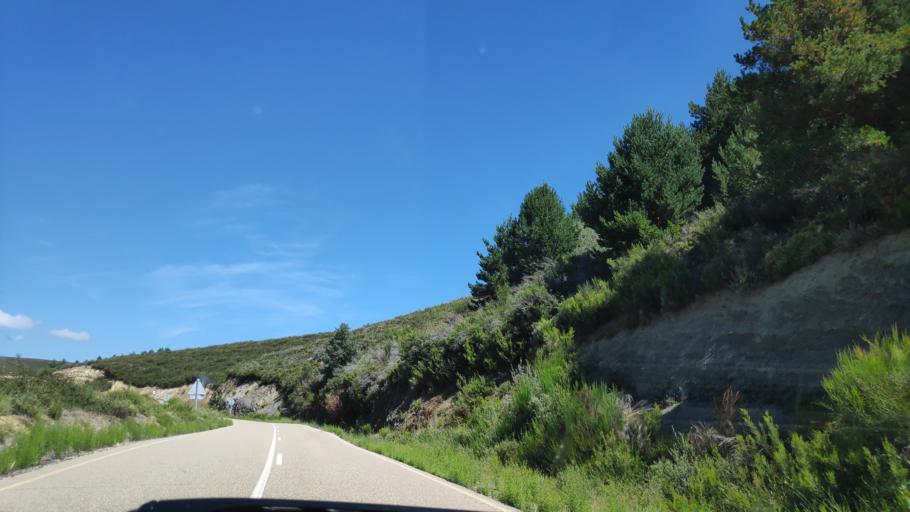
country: ES
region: Castille and Leon
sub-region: Provincia de Zamora
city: Requejo
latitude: 41.9950
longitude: -6.6955
